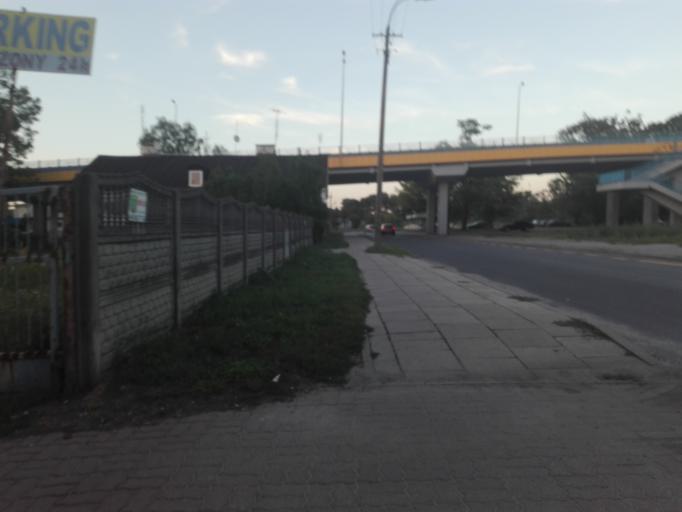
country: PL
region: Masovian Voivodeship
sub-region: Powiat sochaczewski
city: Sochaczew
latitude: 52.2170
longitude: 20.2408
